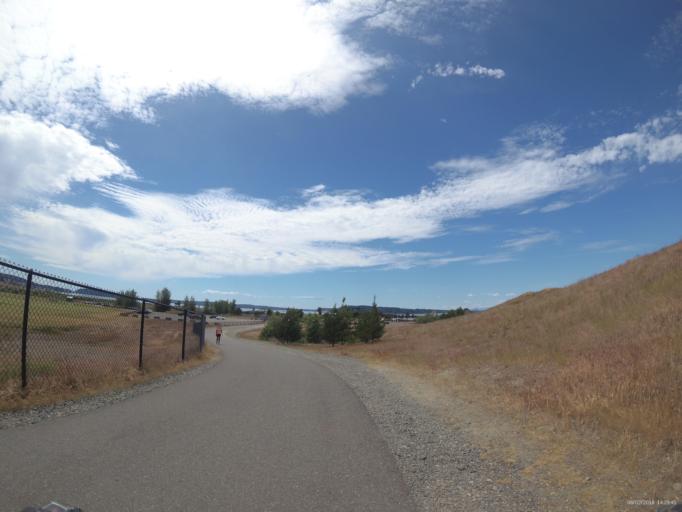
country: US
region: Washington
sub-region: Pierce County
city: University Place
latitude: 47.2016
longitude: -122.5745
